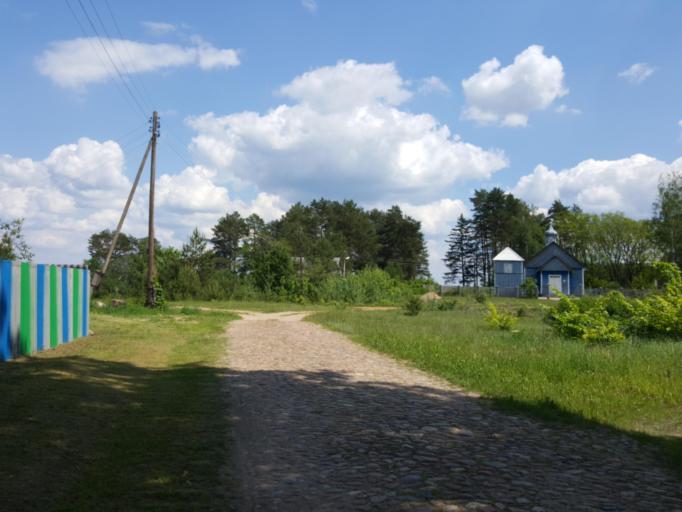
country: BY
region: Brest
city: Kamyanyuki
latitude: 52.5331
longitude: 23.6972
